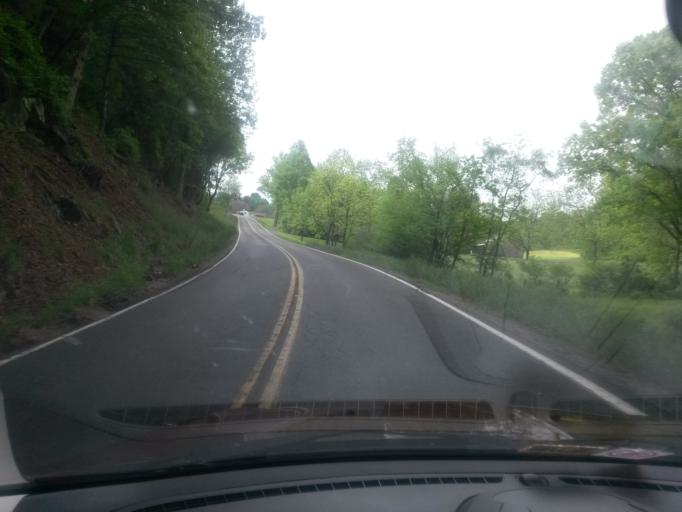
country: US
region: Virginia
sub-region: Floyd County
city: Floyd
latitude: 36.8687
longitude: -80.3342
